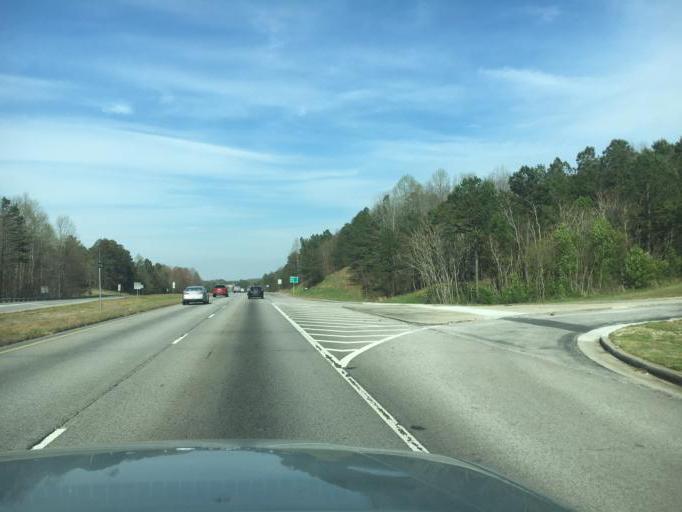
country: US
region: Georgia
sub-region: Hall County
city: Lula
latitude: 34.3953
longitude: -83.6905
